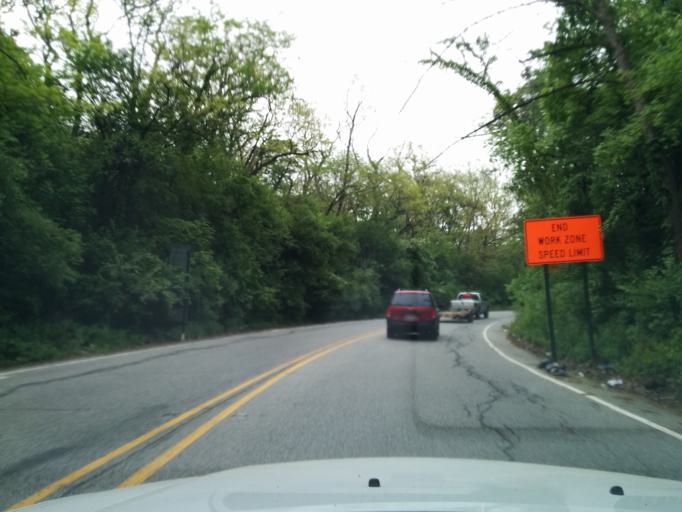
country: US
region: Illinois
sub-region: Cook County
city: Willow Springs
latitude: 41.7315
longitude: -87.8764
